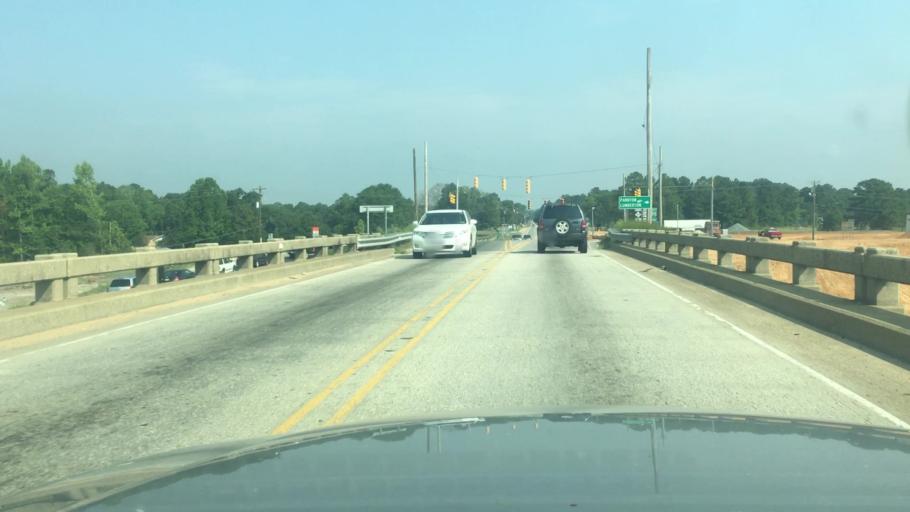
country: US
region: North Carolina
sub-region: Cumberland County
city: Hope Mills
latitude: 34.9449
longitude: -78.9311
